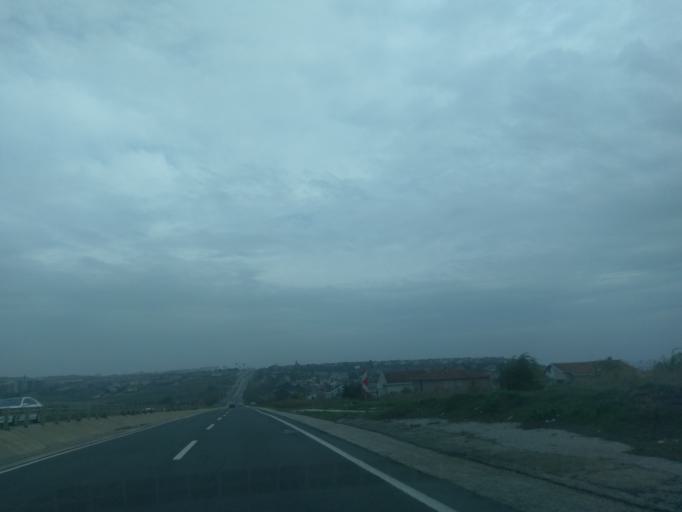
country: TR
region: Istanbul
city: Silivri
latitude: 41.0774
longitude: 28.1788
